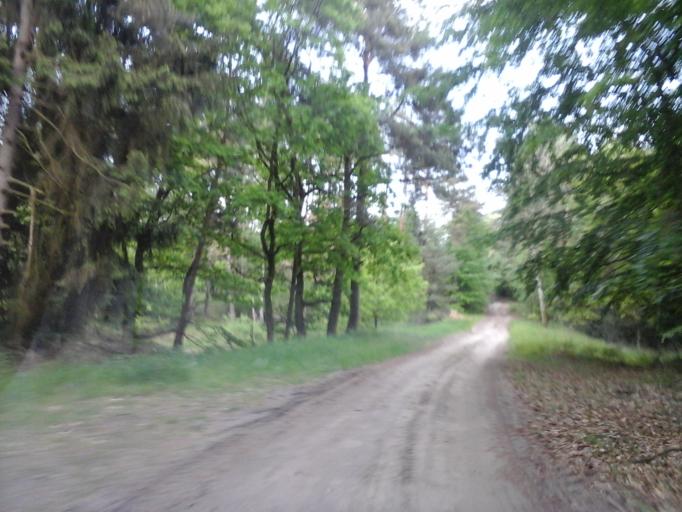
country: PL
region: West Pomeranian Voivodeship
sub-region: Powiat choszczenski
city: Pelczyce
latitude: 52.9778
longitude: 15.3625
